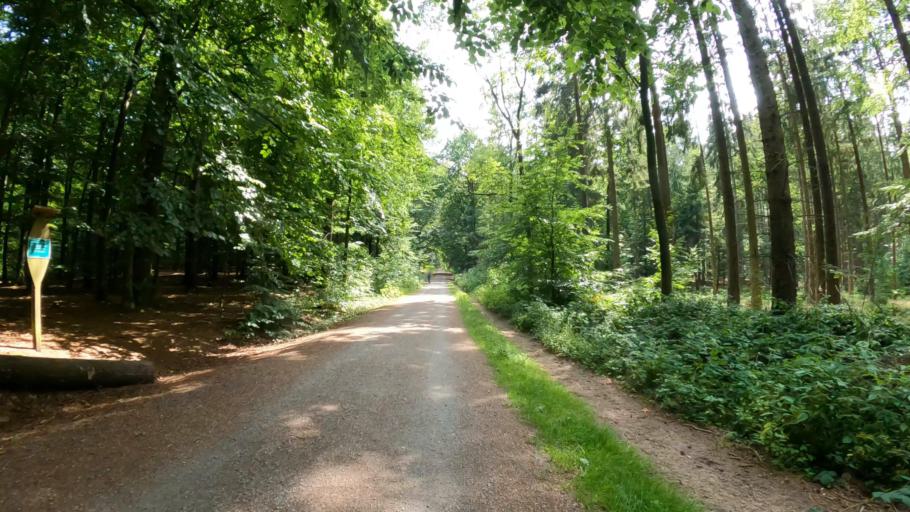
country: DE
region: Schleswig-Holstein
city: Huttblek
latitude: 53.8095
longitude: 10.0731
